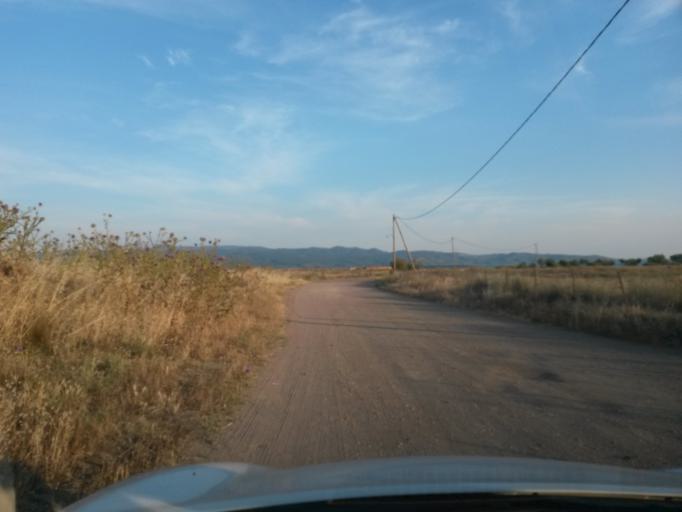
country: GR
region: North Aegean
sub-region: Nomos Lesvou
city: Kalloni
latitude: 39.2088
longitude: 26.2453
